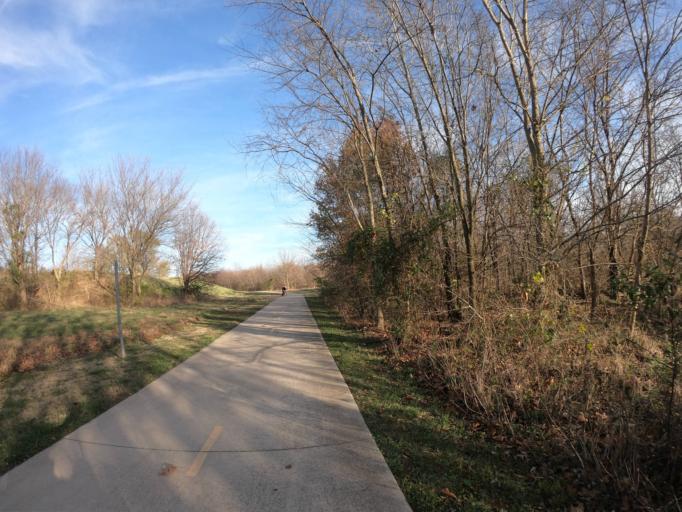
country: US
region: Arkansas
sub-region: Benton County
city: Rogers
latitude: 36.3331
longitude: -94.1651
